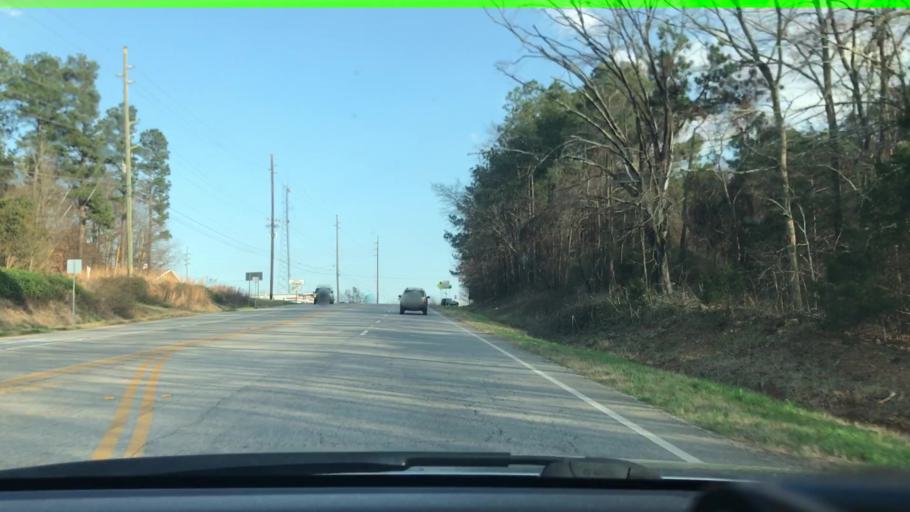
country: US
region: Georgia
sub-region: Oglethorpe County
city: Lexington
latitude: 33.8874
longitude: -83.1297
